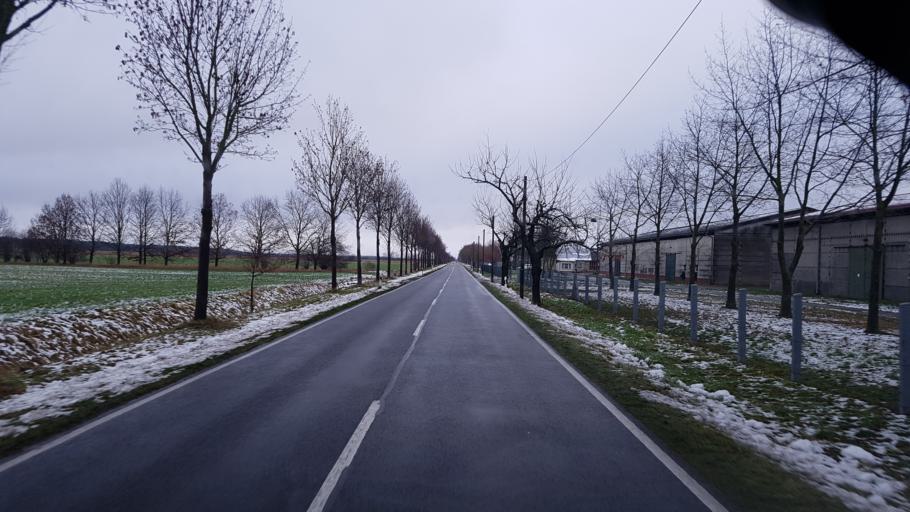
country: DE
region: Brandenburg
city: Luckau
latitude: 51.8500
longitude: 13.7535
